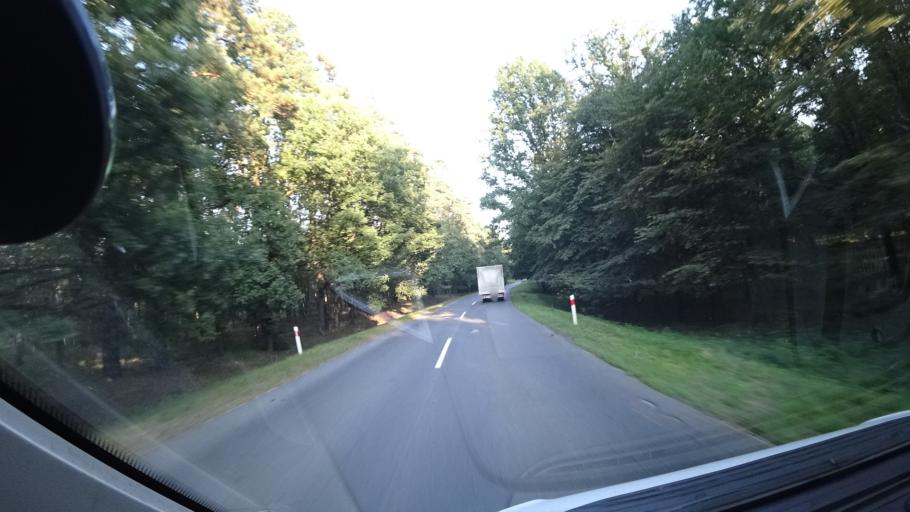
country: PL
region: Opole Voivodeship
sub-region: Powiat kedzierzynsko-kozielski
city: Dziergowice
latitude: 50.2797
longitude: 18.3585
